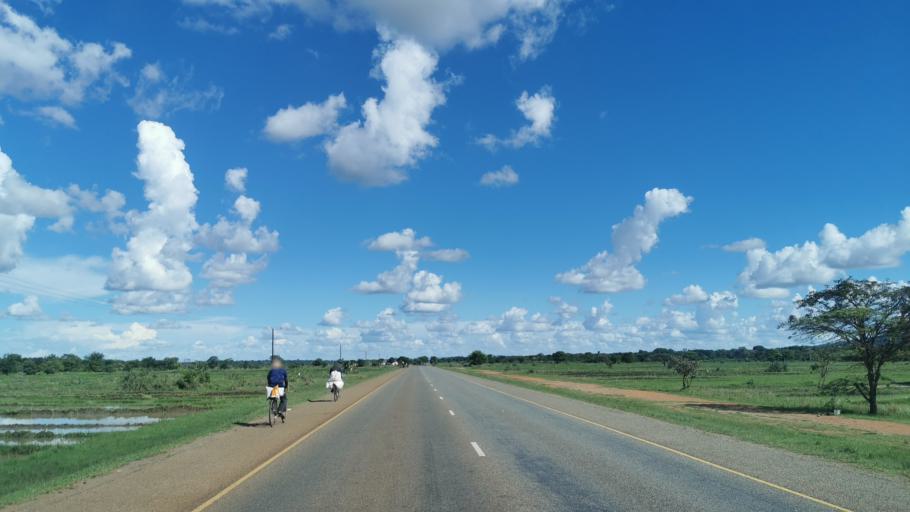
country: TZ
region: Geita
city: Ushirombo
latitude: -3.4793
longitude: 31.9212
